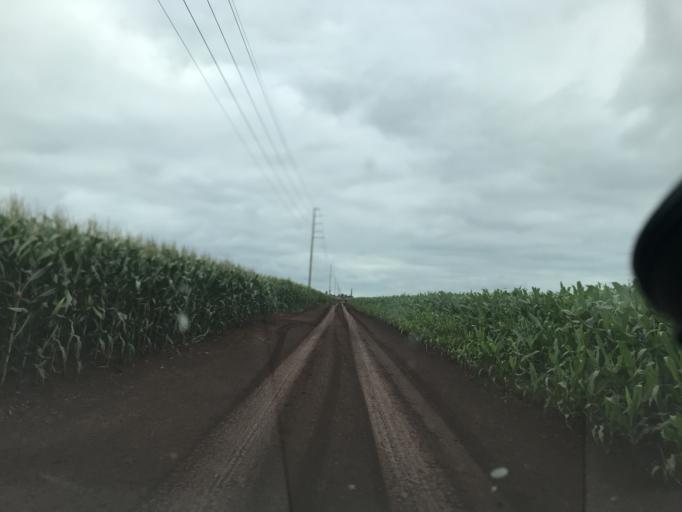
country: BR
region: Parana
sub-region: Palotina
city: Palotina
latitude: -24.3034
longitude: -53.8206
